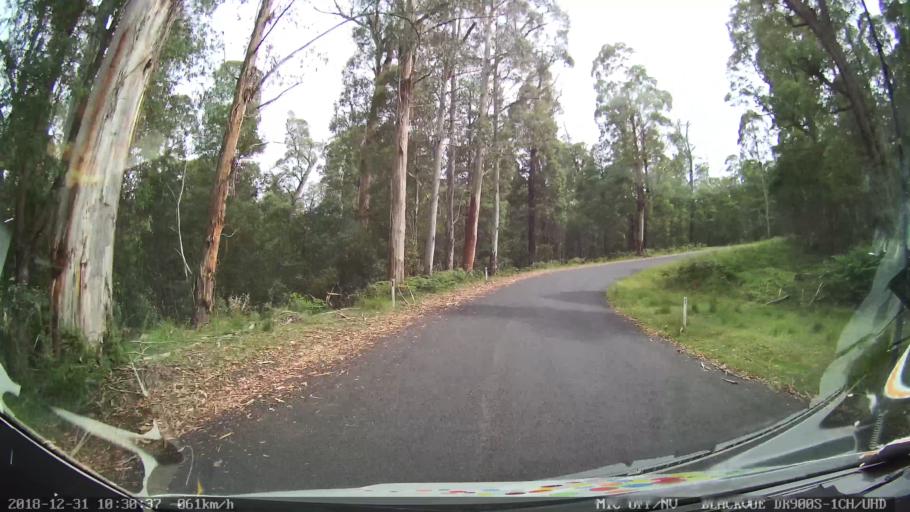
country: AU
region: New South Wales
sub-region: Snowy River
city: Jindabyne
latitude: -36.4615
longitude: 148.1507
